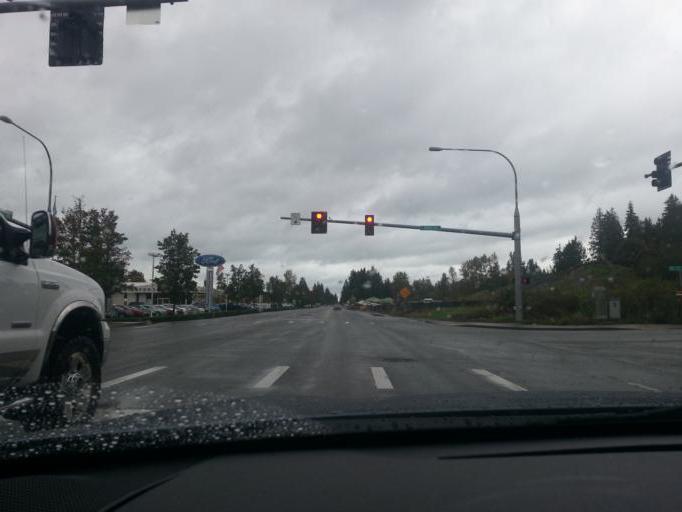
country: US
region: Washington
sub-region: Snohomish County
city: Fobes Hill
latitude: 47.9453
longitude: -122.1105
